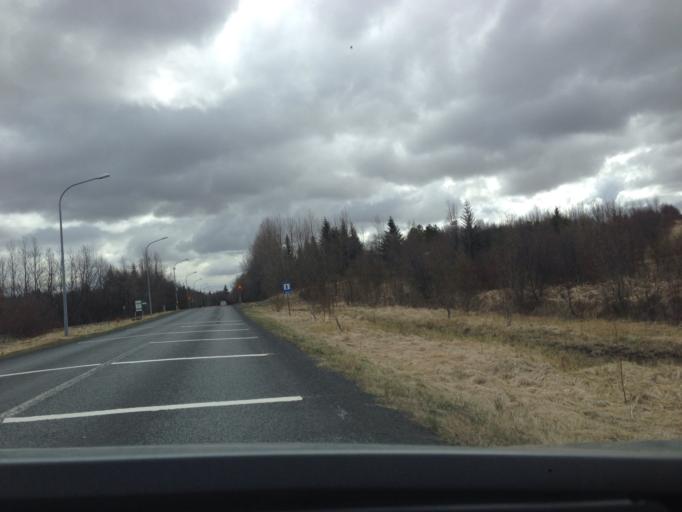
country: IS
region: South
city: Selfoss
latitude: 64.1199
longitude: -20.5030
